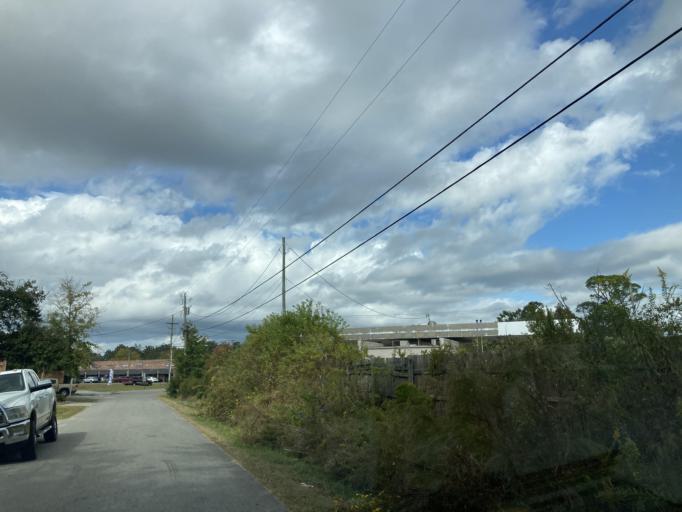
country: US
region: Mississippi
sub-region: Jackson County
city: Gulf Hills
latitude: 30.4360
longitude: -88.8325
